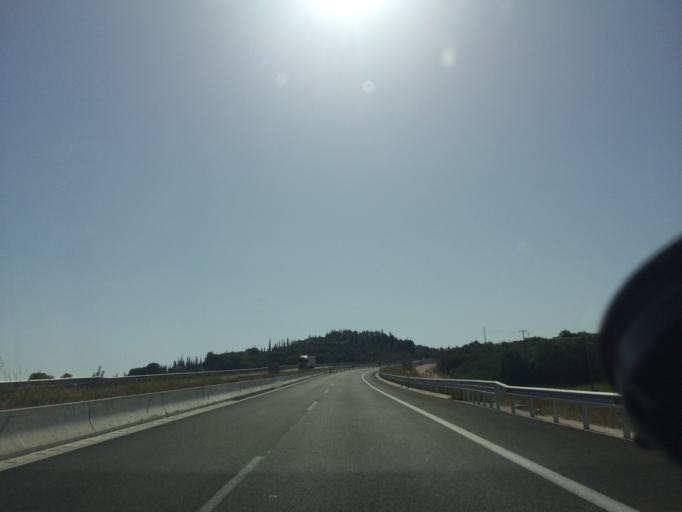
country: GR
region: Thessaly
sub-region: Nomos Larisis
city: Pyrgetos
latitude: 39.9675
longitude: 22.6423
